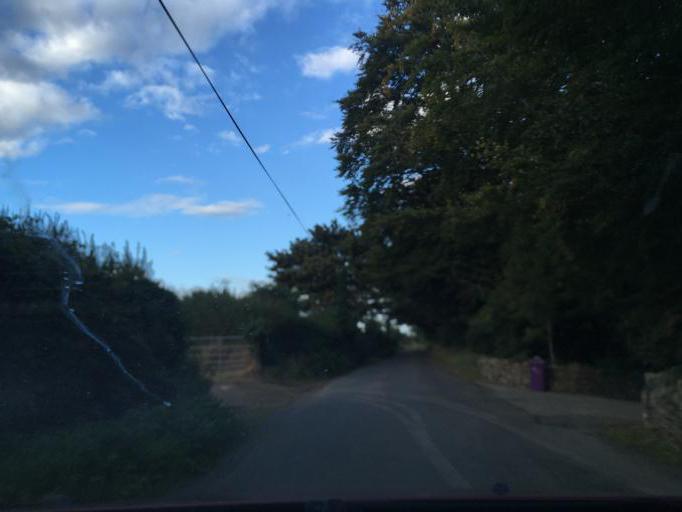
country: IE
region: Leinster
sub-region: Wicklow
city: Wicklow
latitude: 52.9286
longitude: -6.0804
